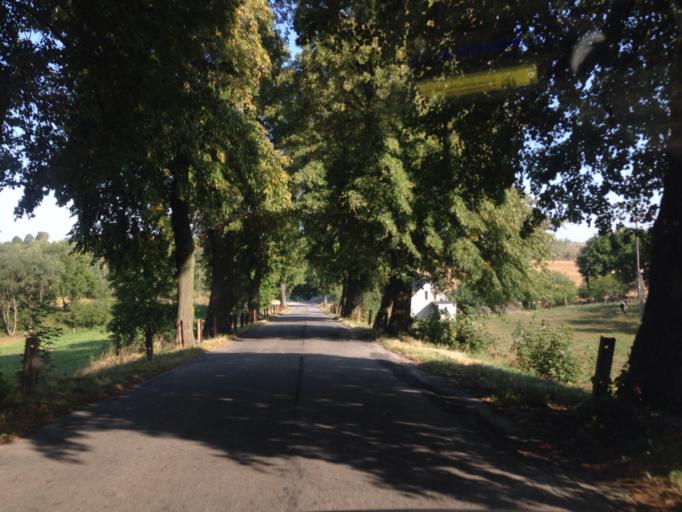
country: PL
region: Kujawsko-Pomorskie
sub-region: Powiat brodnicki
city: Brzozie
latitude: 53.3017
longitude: 19.6149
